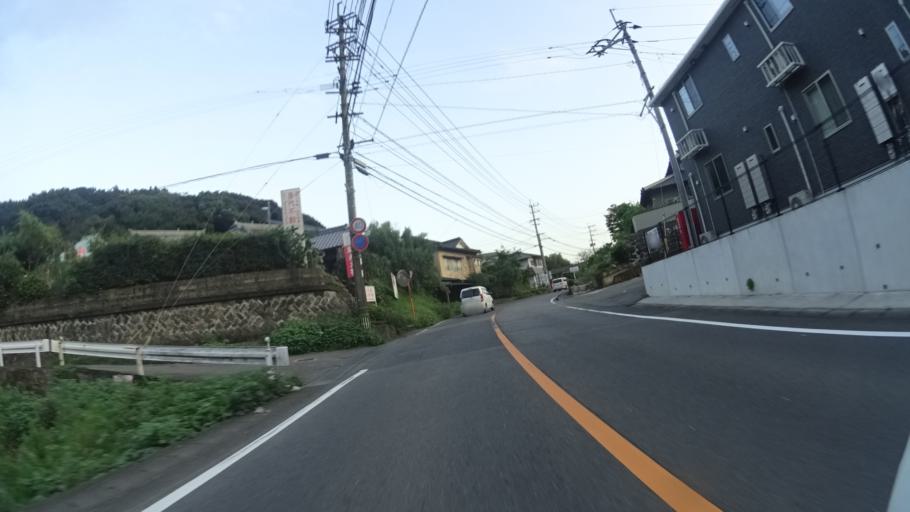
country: JP
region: Oita
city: Beppu
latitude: 33.3202
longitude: 131.4807
